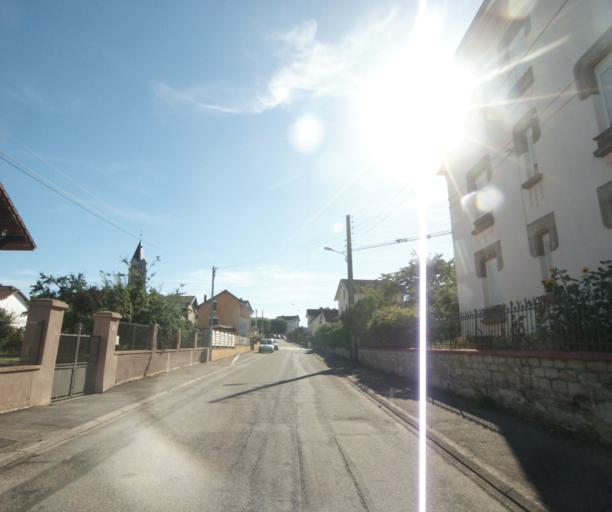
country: FR
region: Lorraine
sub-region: Departement des Vosges
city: Chantraine
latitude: 48.1737
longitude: 6.4362
